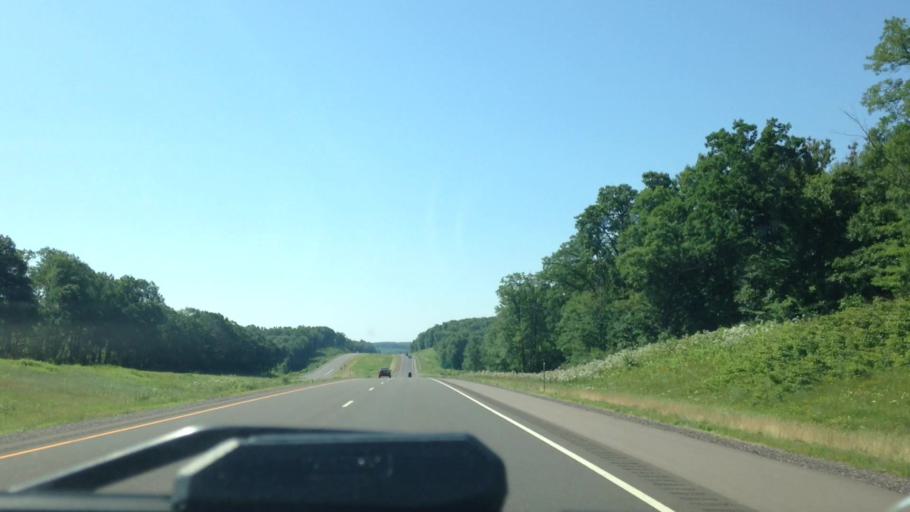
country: US
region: Wisconsin
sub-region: Washburn County
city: Spooner
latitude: 46.0025
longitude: -91.8332
